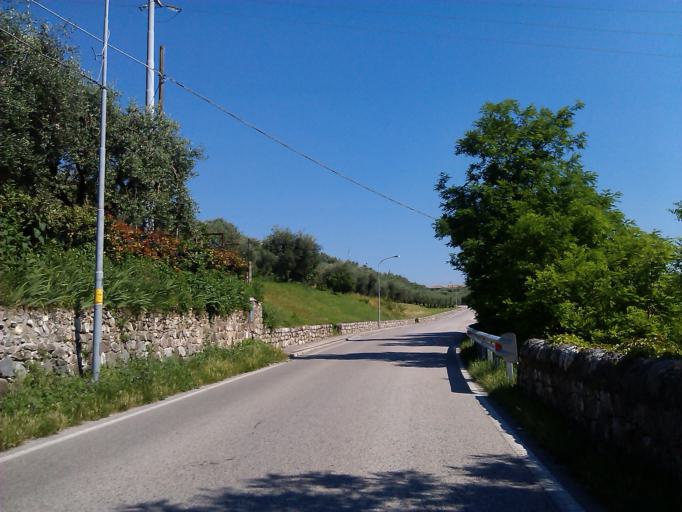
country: IT
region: Veneto
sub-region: Provincia di Vicenza
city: Pove del Grappa
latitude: 45.8007
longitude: 11.7231
